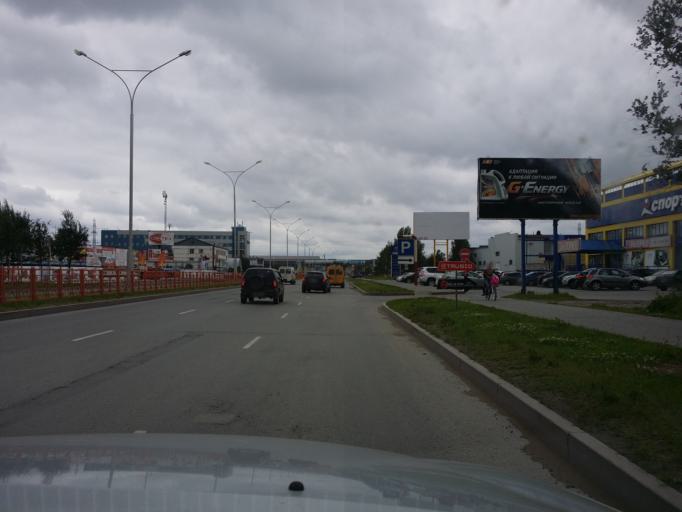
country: RU
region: Khanty-Mansiyskiy Avtonomnyy Okrug
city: Nizhnevartovsk
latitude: 60.9392
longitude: 76.5382
